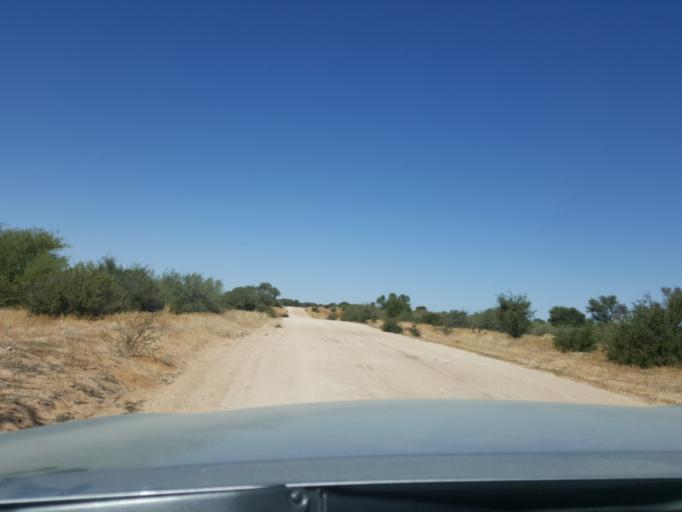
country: BW
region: Kgalagadi
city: Hukuntsi
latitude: -23.9788
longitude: 21.2075
